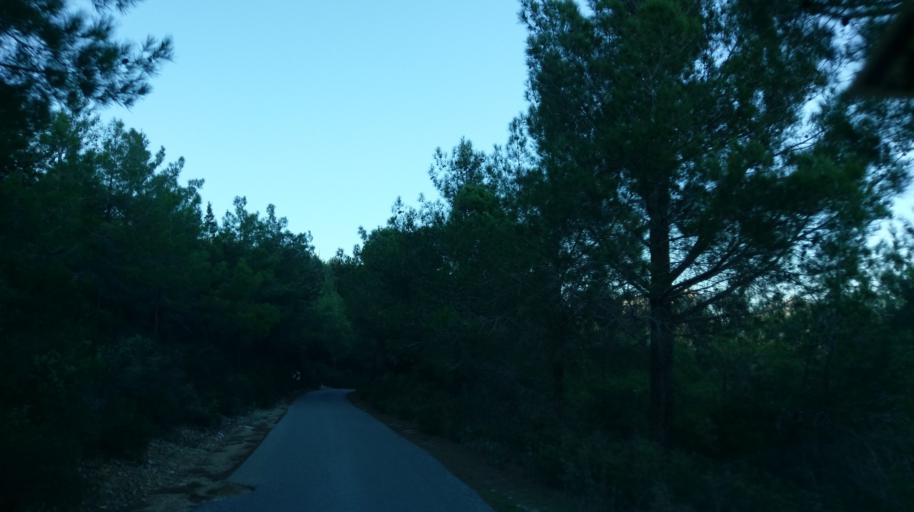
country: CY
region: Ammochostos
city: Trikomo
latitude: 35.3910
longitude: 33.9027
